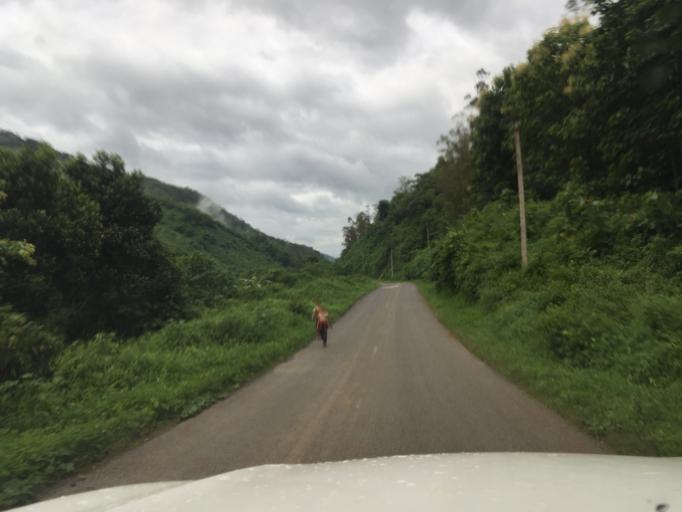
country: LA
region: Oudomxai
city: Muang La
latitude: 20.9979
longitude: 102.2317
